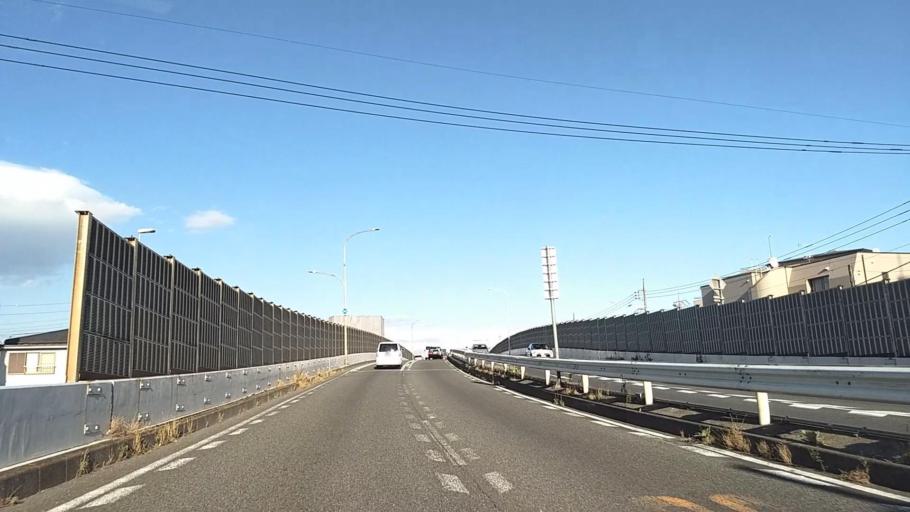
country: JP
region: Tokyo
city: Chofugaoka
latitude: 35.6055
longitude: 139.6090
